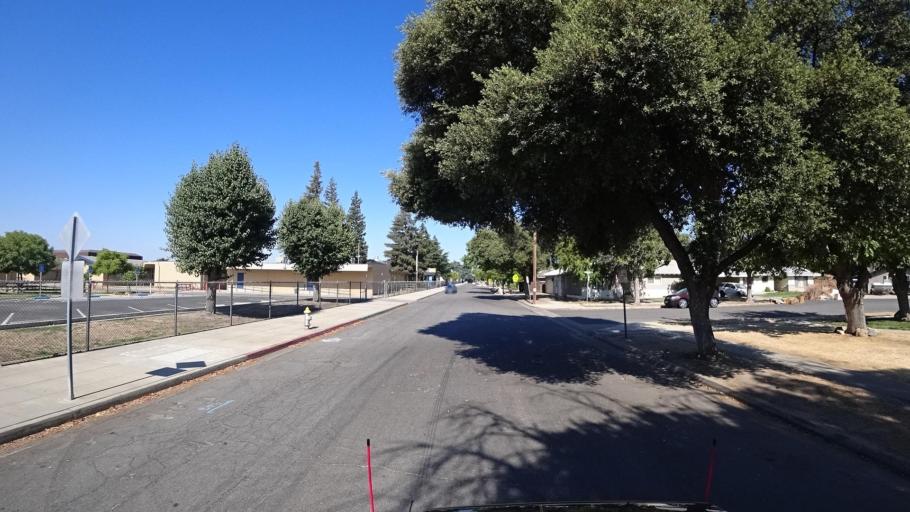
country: US
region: California
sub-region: Fresno County
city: Fresno
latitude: 36.7850
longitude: -119.7508
